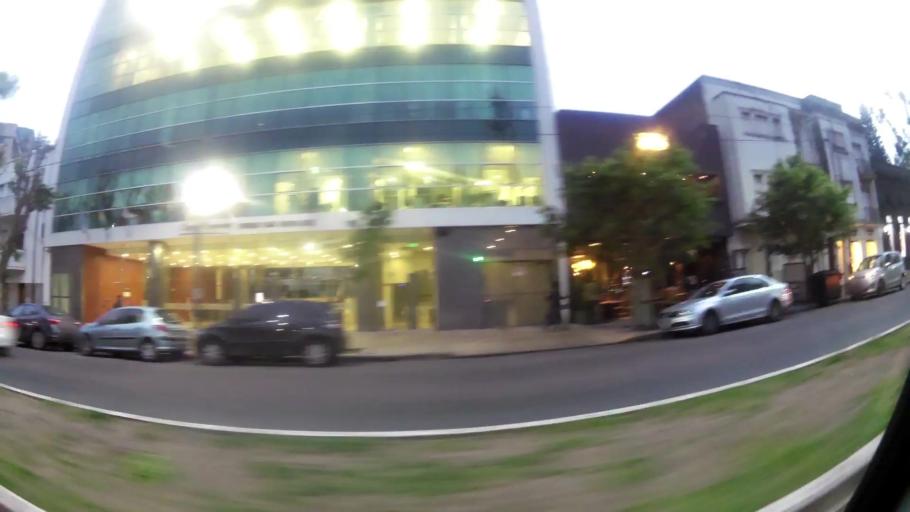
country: AR
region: Buenos Aires
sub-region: Partido de La Plata
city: La Plata
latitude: -34.9150
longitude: -57.9550
